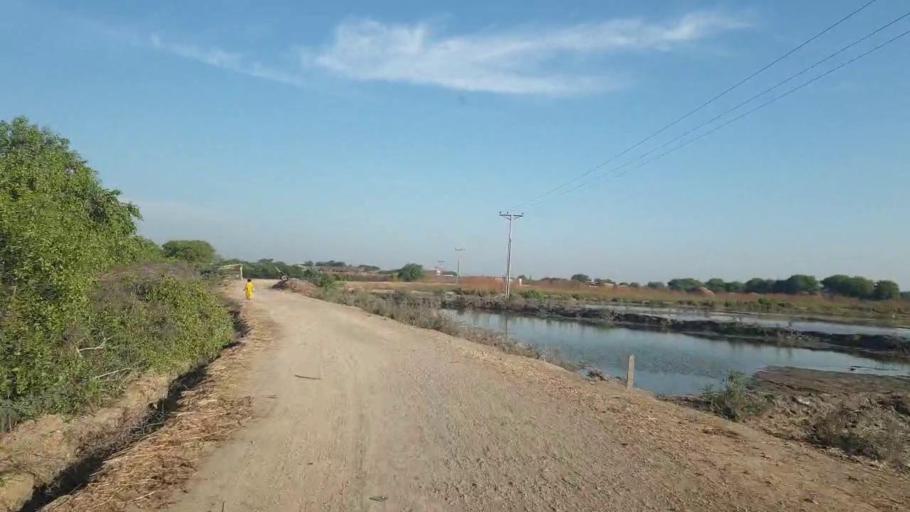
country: PK
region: Sindh
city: Talhar
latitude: 24.8137
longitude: 68.8394
